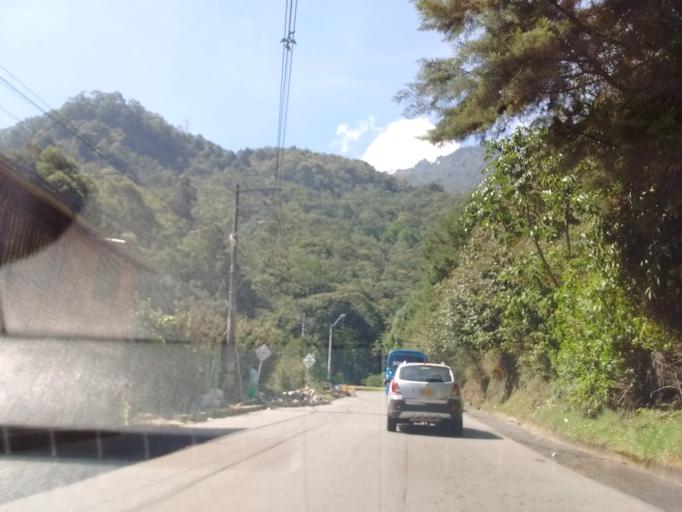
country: CO
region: Antioquia
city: Medellin
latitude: 6.2273
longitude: -75.5239
